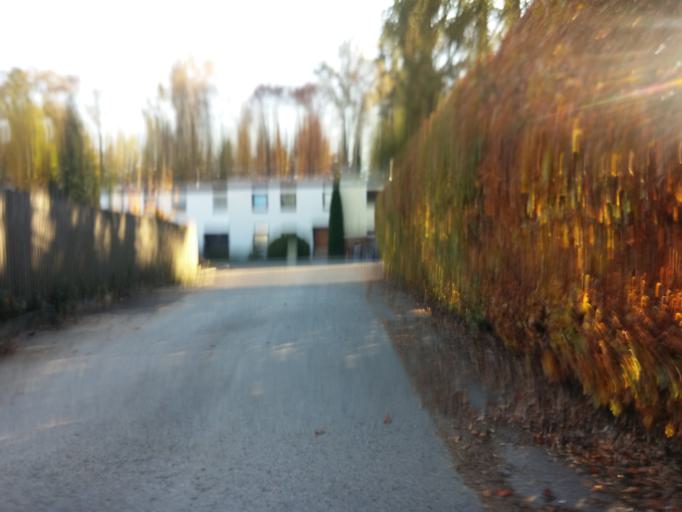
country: DE
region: Bavaria
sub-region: Upper Bavaria
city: Vaterstetten
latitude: 48.0916
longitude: 11.7904
